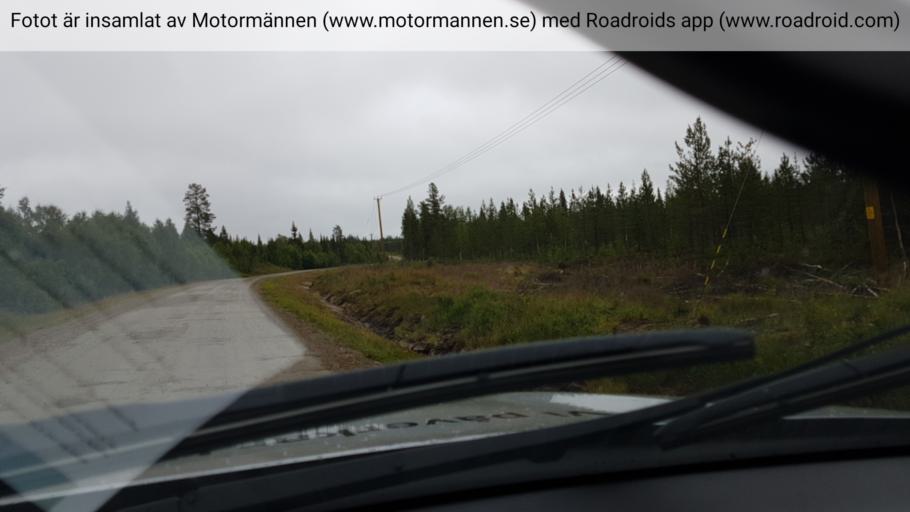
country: SE
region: Norrbotten
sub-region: Gallivare Kommun
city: Gaellivare
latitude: 66.7162
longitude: 20.5003
